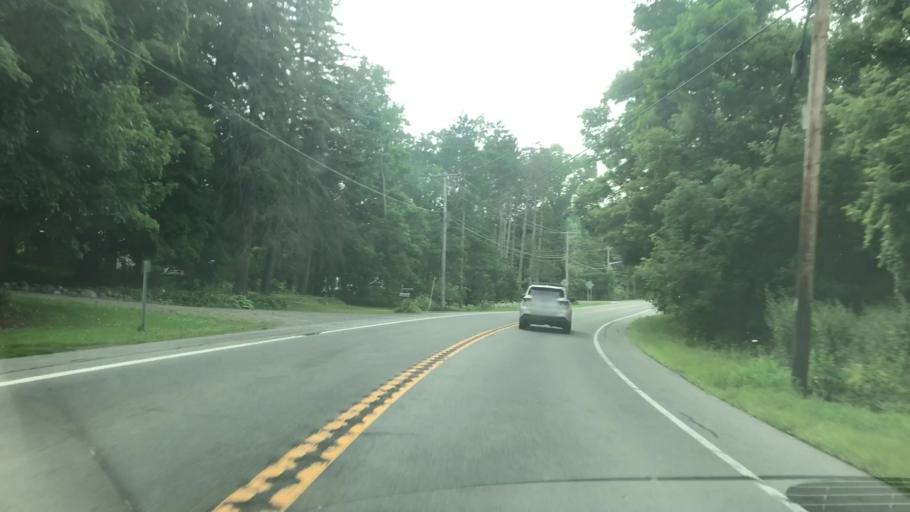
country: US
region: New York
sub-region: Monroe County
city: Fairport
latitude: 43.1278
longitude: -77.4206
